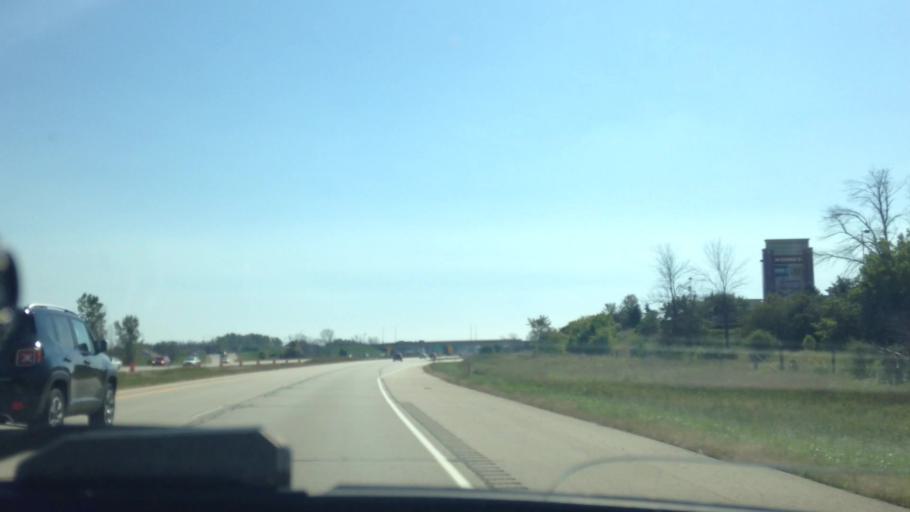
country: US
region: Wisconsin
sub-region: Ozaukee County
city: Grafton
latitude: 43.3250
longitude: -87.9198
